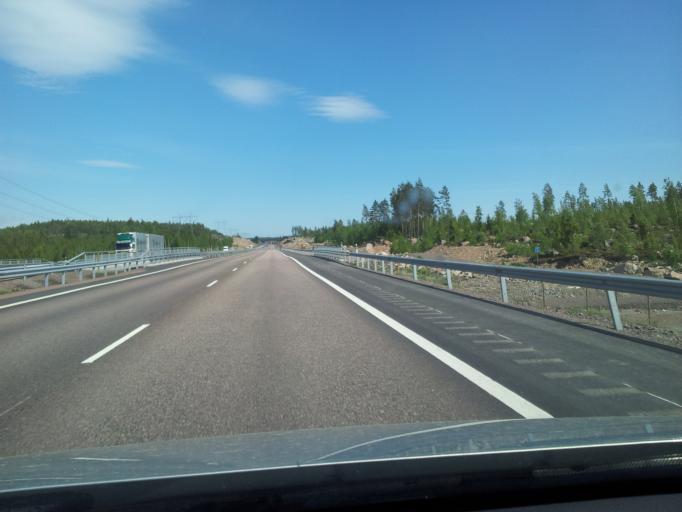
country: FI
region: Uusimaa
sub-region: Loviisa
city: Lovisa
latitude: 60.4895
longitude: 26.3418
